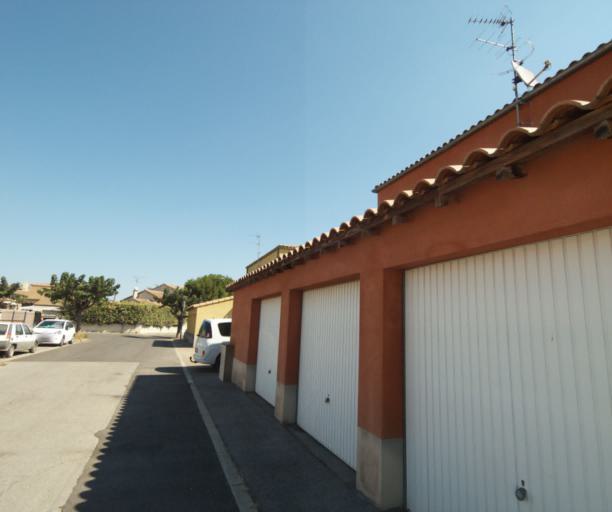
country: FR
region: Languedoc-Roussillon
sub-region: Departement de l'Herault
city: Marsillargues
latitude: 43.6656
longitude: 4.1691
